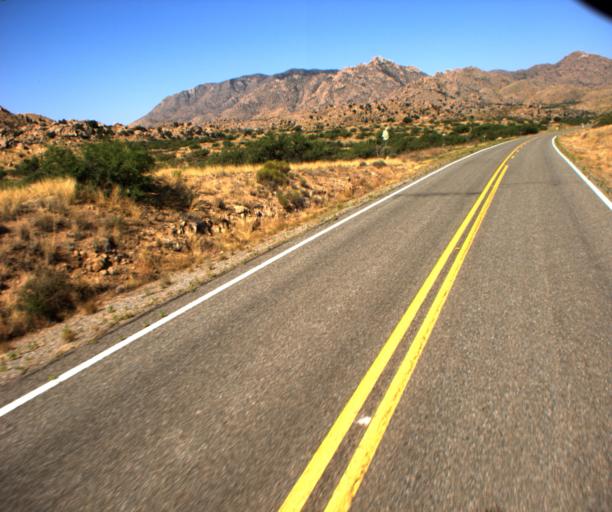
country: US
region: Arizona
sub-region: Graham County
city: Swift Trail Junction
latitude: 32.5604
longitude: -109.7440
